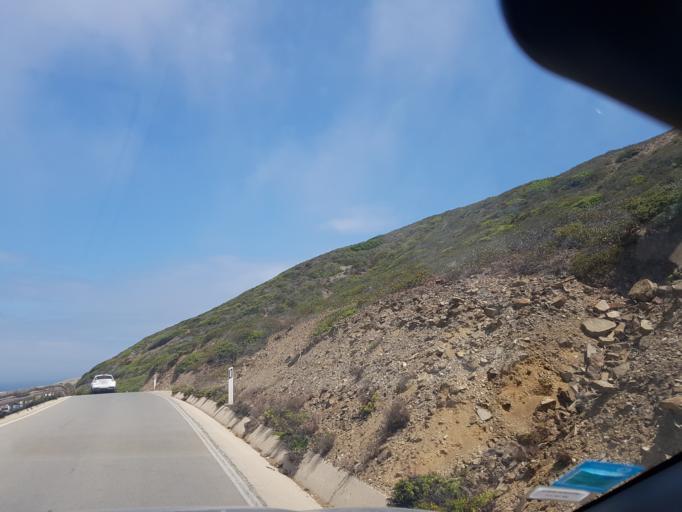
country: PT
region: Faro
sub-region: Vila do Bispo
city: Vila do Bispo
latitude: 37.1068
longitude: -8.9340
